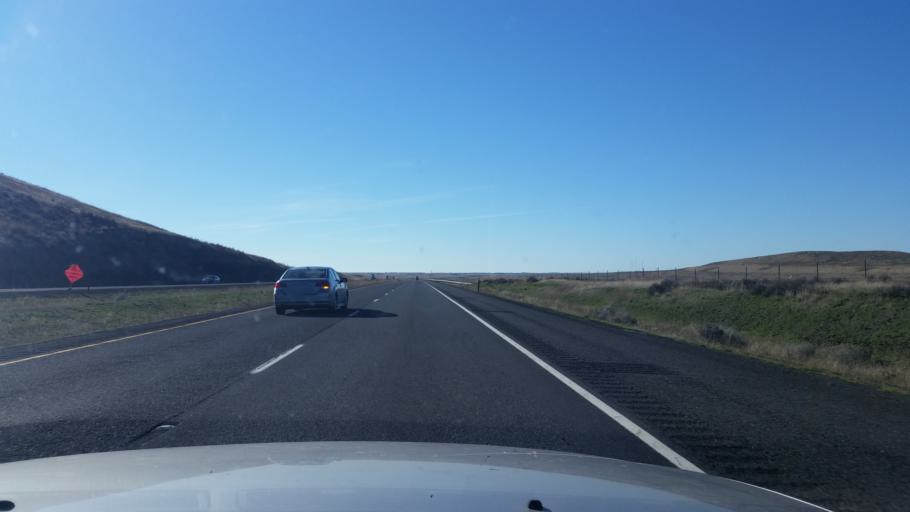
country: US
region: Washington
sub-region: Spokane County
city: Medical Lake
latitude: 47.3515
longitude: -117.8980
